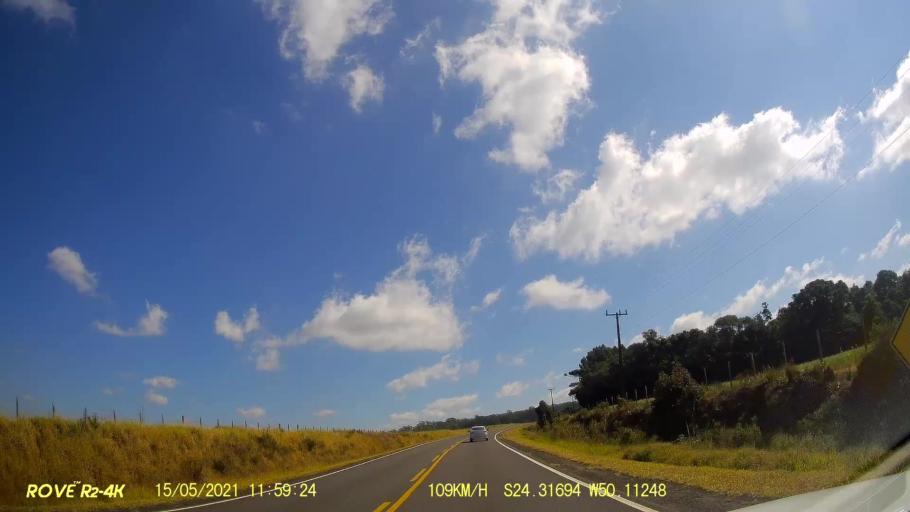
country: BR
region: Parana
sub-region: Pirai Do Sul
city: Pirai do Sul
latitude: -24.3172
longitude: -50.1123
